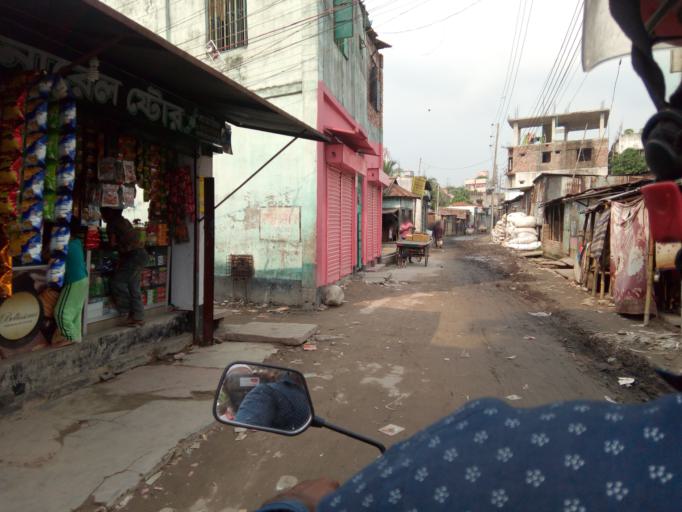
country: BD
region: Dhaka
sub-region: Dhaka
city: Dhaka
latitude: 23.7036
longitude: 90.4563
